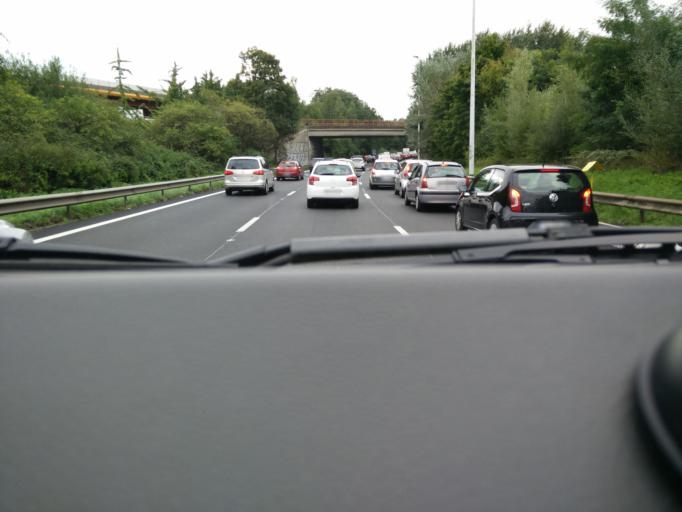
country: FR
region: Nord-Pas-de-Calais
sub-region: Departement du Nord
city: Wasquehal
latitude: 50.6602
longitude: 3.1151
